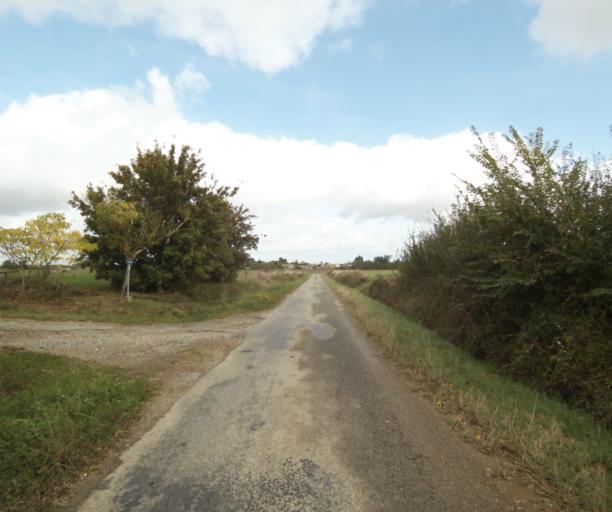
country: FR
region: Midi-Pyrenees
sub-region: Departement du Tarn-et-Garonne
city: Finhan
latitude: 43.8911
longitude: 1.1230
